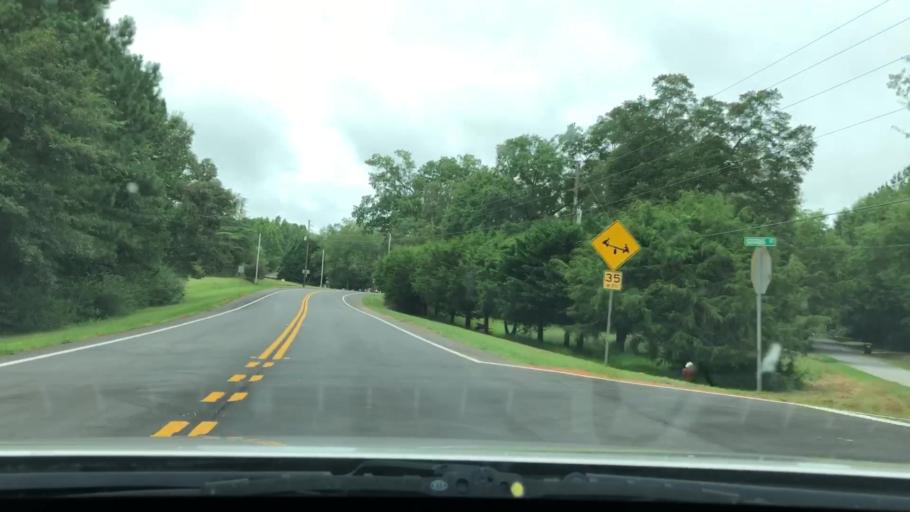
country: US
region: Georgia
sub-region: Upson County
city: Hannahs Mill
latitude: 33.0120
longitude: -84.4949
